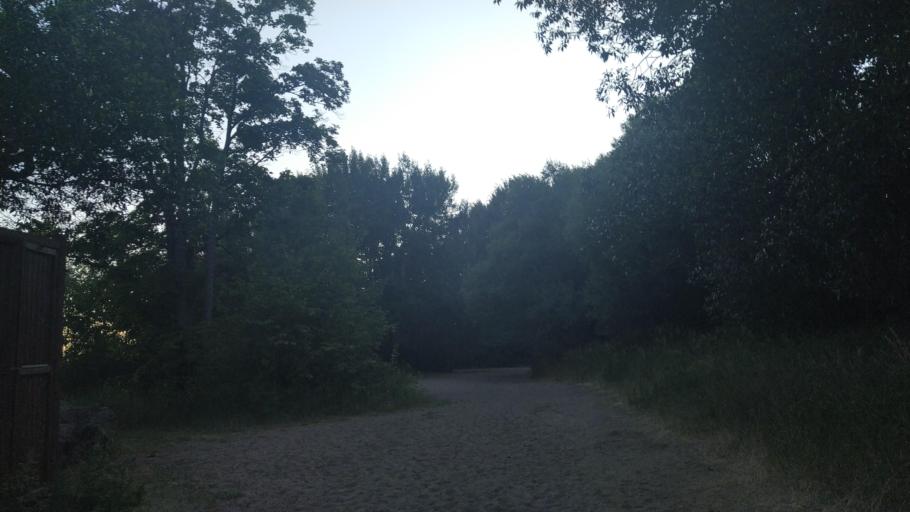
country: RU
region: St.-Petersburg
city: Kronshtadt
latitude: 60.0242
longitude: 29.6734
